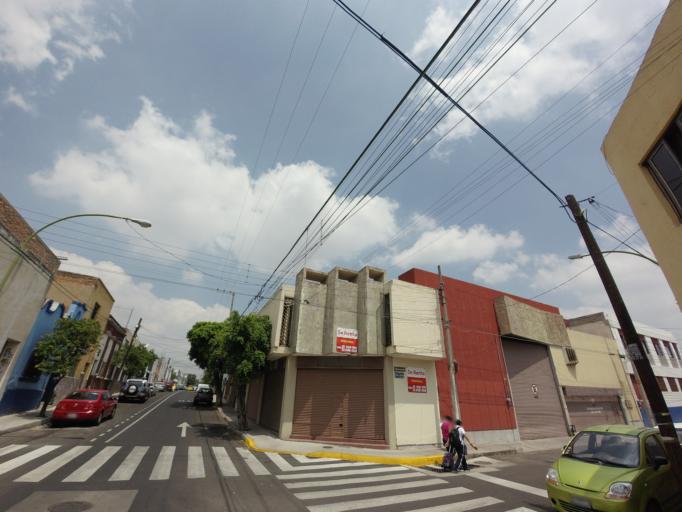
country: MX
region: Jalisco
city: Guadalajara
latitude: 20.6831
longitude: -103.3424
